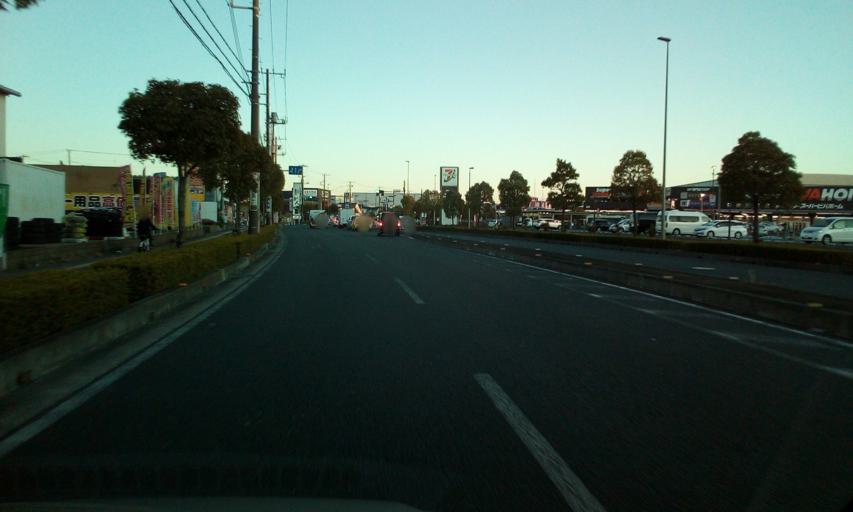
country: JP
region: Saitama
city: Yashio-shi
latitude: 35.8439
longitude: 139.8562
